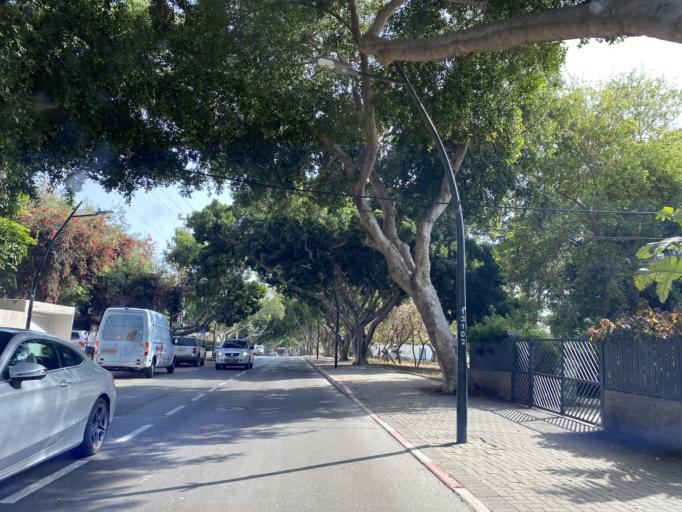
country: IL
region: Tel Aviv
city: Herzliya Pituah
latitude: 32.1717
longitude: 34.8073
